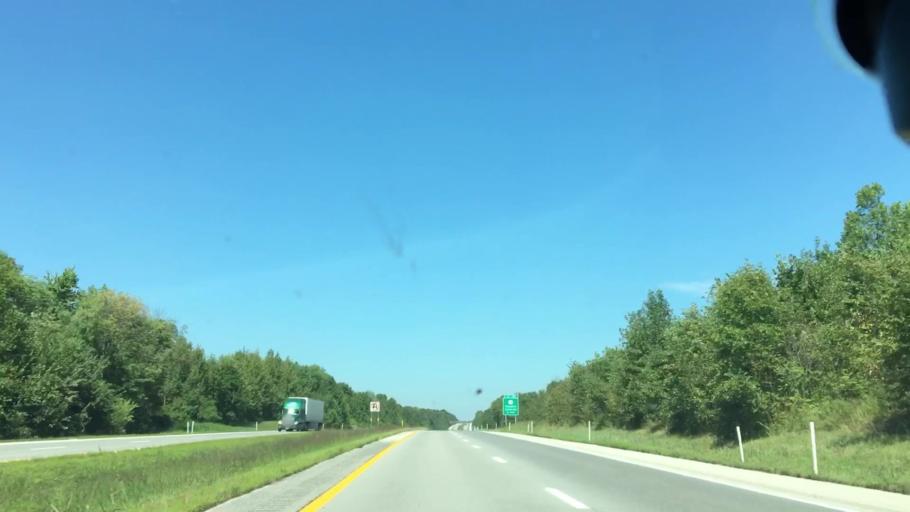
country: US
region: Kentucky
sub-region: Webster County
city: Sebree
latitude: 37.6561
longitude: -87.5128
